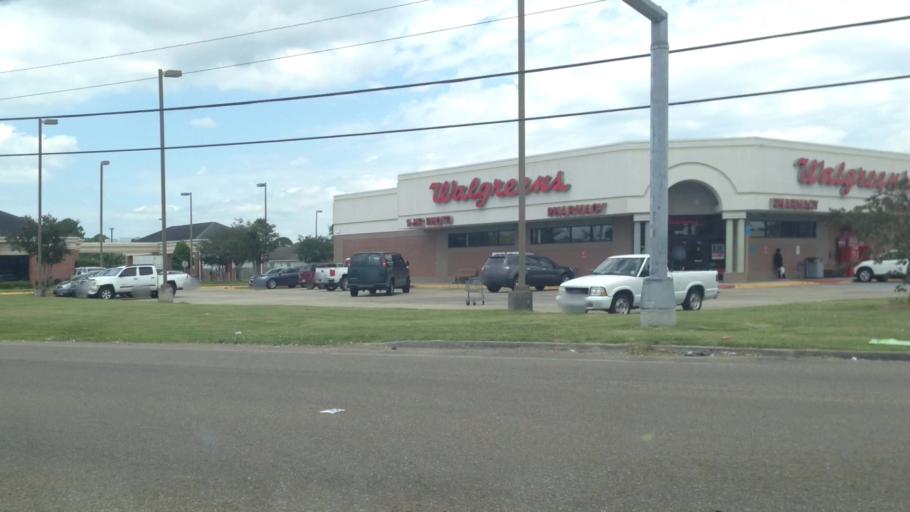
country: US
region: Louisiana
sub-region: Iberia Parish
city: New Iberia
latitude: 29.9857
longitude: -91.8209
